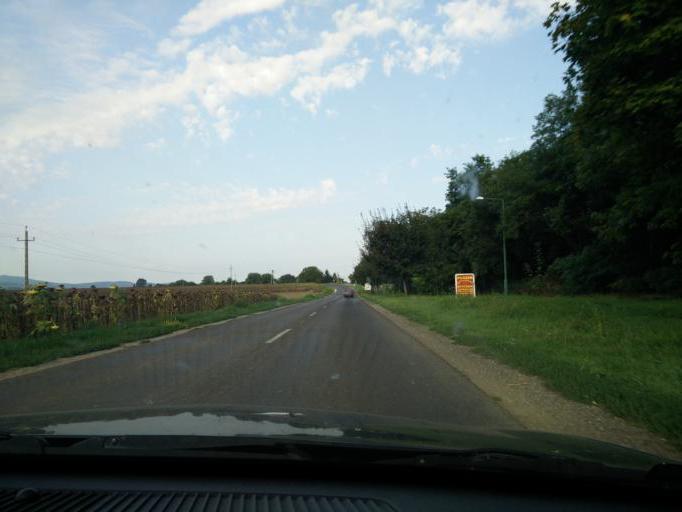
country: HU
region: Tolna
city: Bonyhad
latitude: 46.2992
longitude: 18.5032
